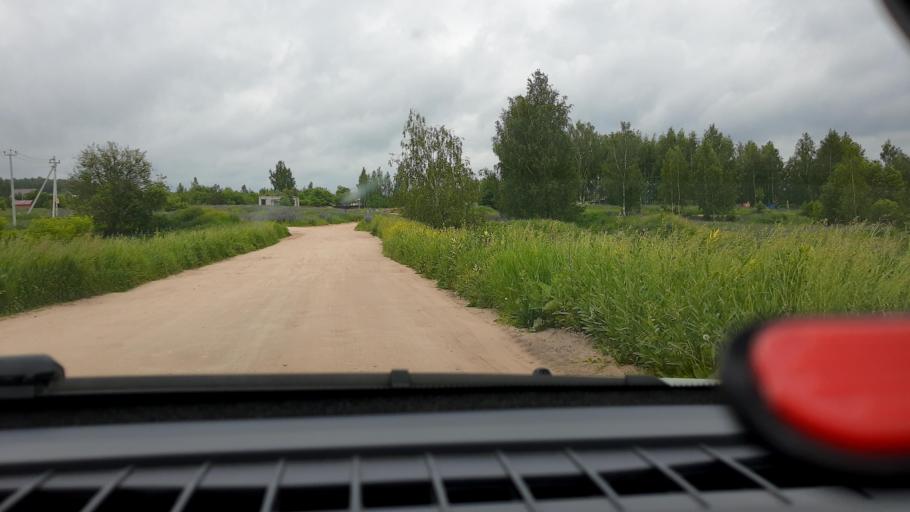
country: RU
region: Nizjnij Novgorod
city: Burevestnik
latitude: 56.1032
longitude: 43.9473
